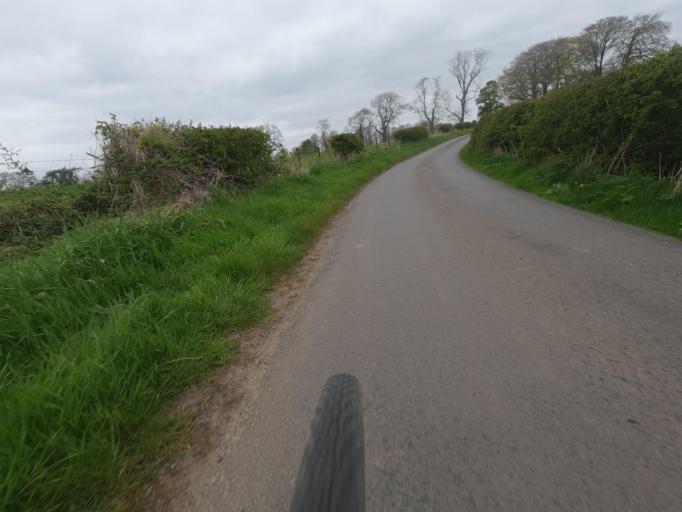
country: GB
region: England
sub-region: Northumberland
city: Meldon
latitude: 55.0672
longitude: -1.8337
